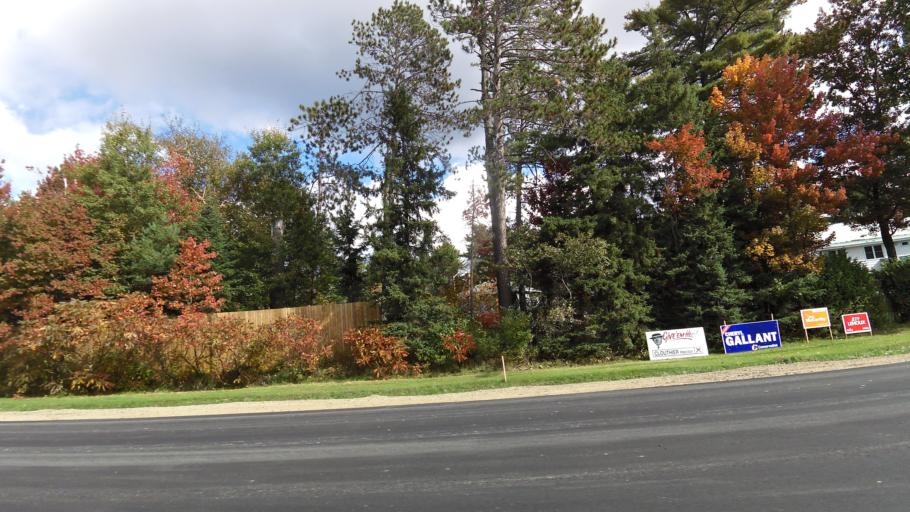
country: CA
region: Ontario
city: Deep River
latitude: 46.0994
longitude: -77.4977
